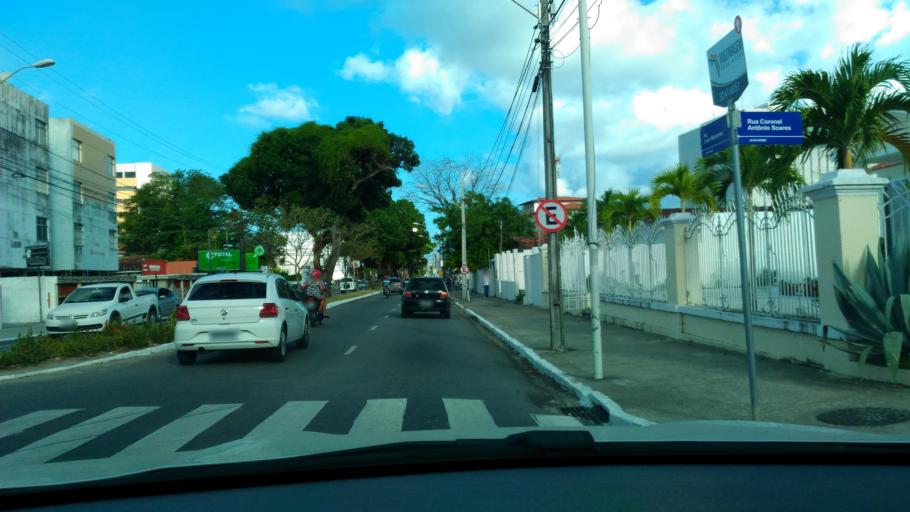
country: BR
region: Paraiba
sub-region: Joao Pessoa
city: Joao Pessoa
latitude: -7.1260
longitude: -34.8814
